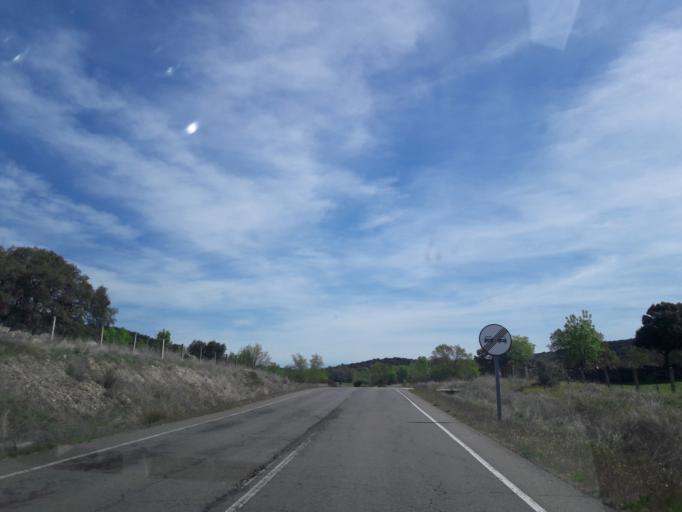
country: ES
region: Castille and Leon
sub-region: Provincia de Salamanca
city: Fuentes de Bejar
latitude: 40.4960
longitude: -5.7115
